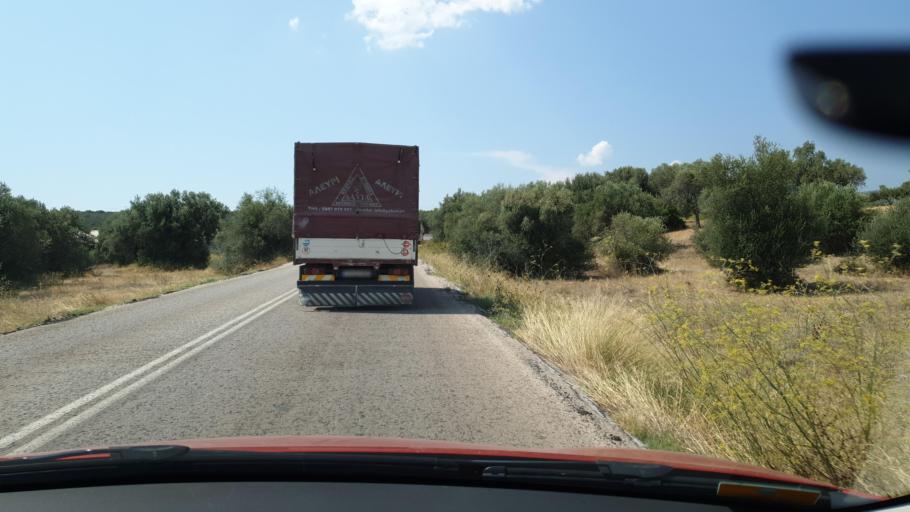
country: GR
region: Central Greece
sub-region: Nomos Evvoias
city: Psachna
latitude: 38.5817
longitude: 23.6113
